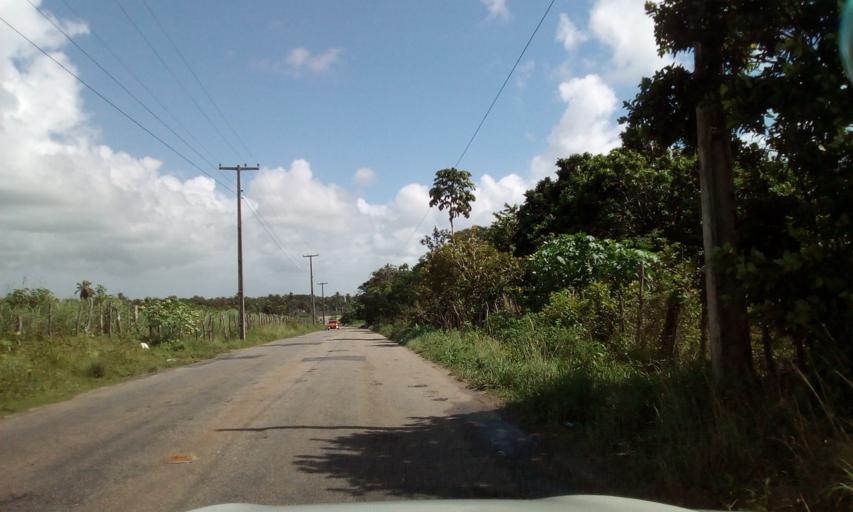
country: BR
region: Paraiba
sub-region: Conde
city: Conde
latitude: -7.2221
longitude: -34.8278
